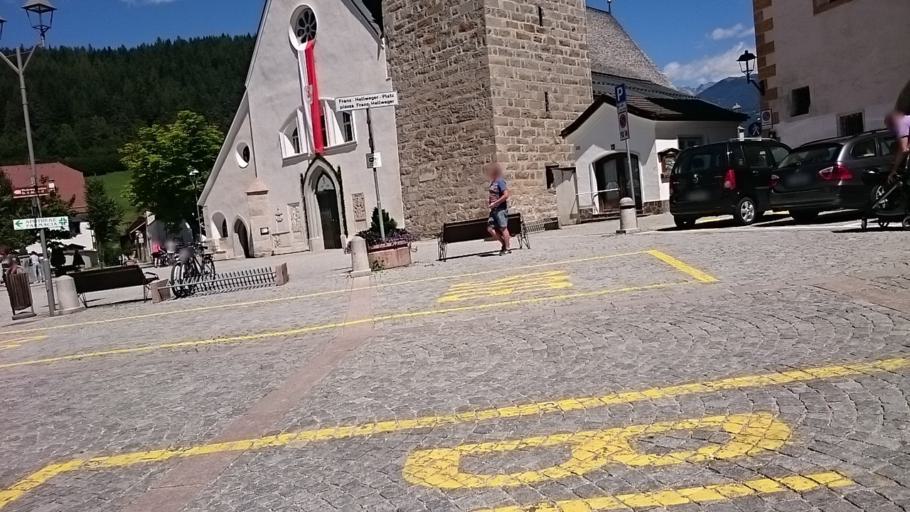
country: IT
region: Trentino-Alto Adige
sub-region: Bolzano
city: San Lorenzo di Sebato
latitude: 46.7830
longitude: 11.9024
